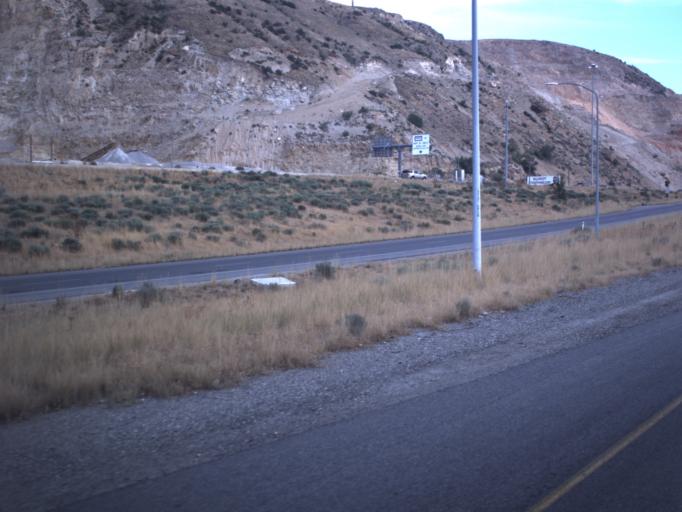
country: US
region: Utah
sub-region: Davis County
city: North Salt Lake
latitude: 40.8299
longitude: -111.9173
